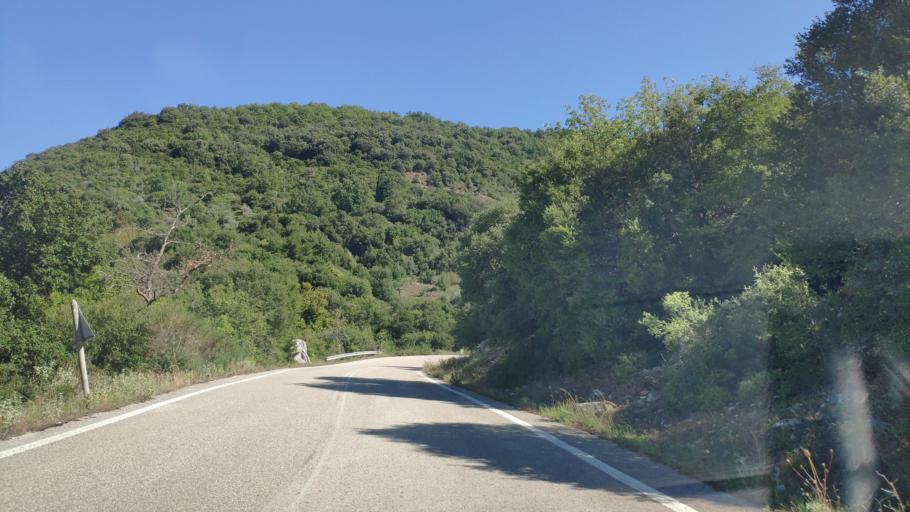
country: GR
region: West Greece
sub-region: Nomos Aitolias kai Akarnanias
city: Sardinia
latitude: 38.9266
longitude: 21.4055
